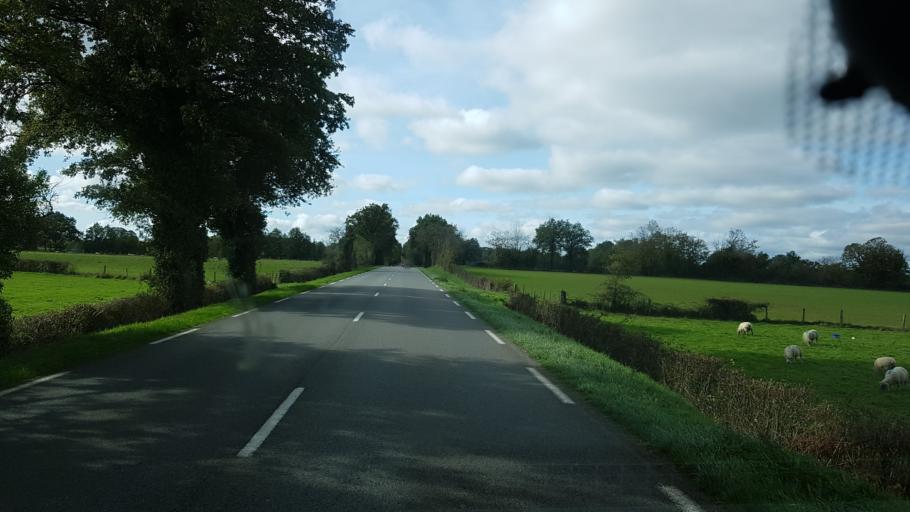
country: FR
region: Poitou-Charentes
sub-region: Departement de la Charente
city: Confolens
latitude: 46.0782
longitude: 0.7868
